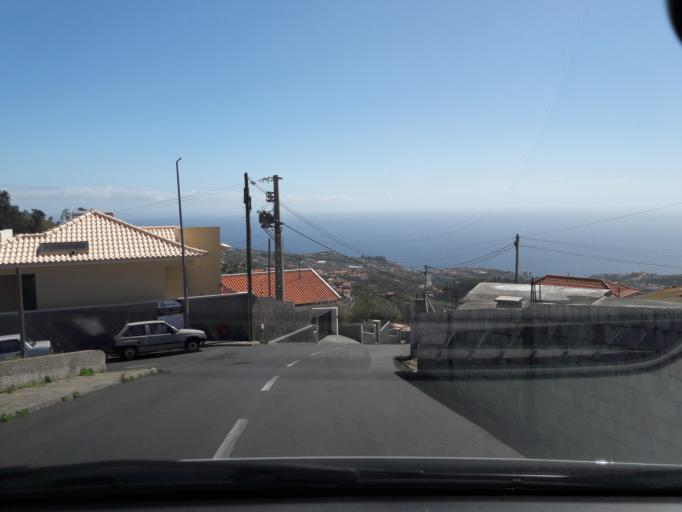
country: PT
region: Madeira
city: Camara de Lobos
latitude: 32.6701
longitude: -16.9548
